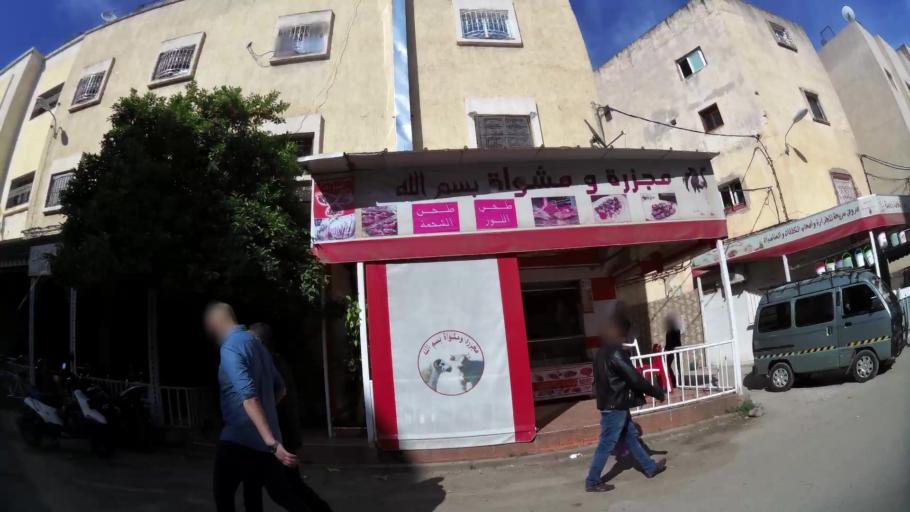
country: MA
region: Fes-Boulemane
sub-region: Fes
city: Fes
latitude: 34.0220
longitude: -5.0359
